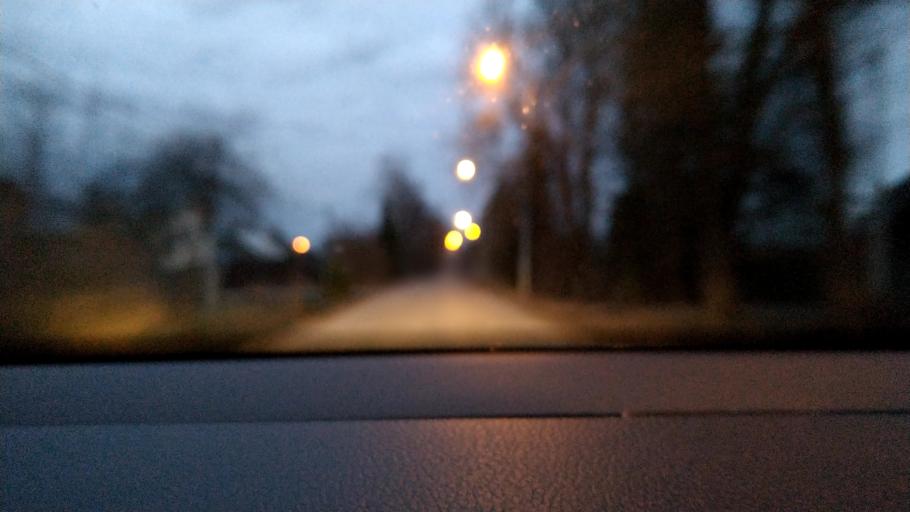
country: RU
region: Moscow
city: Tolstopal'tsevo
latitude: 55.6065
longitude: 37.2113
